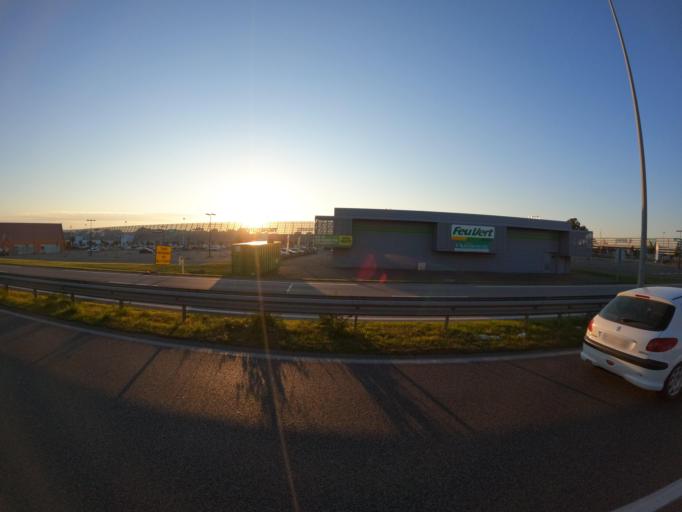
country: FR
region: Pays de la Loire
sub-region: Departement de la Vendee
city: Mouilleron-le-Captif
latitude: 46.7001
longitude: -1.4295
